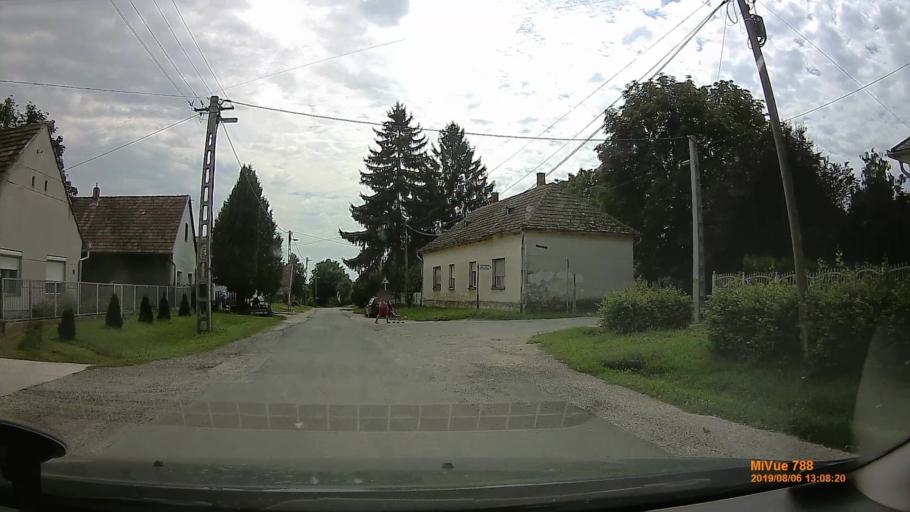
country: HU
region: Zala
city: Pacsa
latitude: 46.6272
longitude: 17.0621
